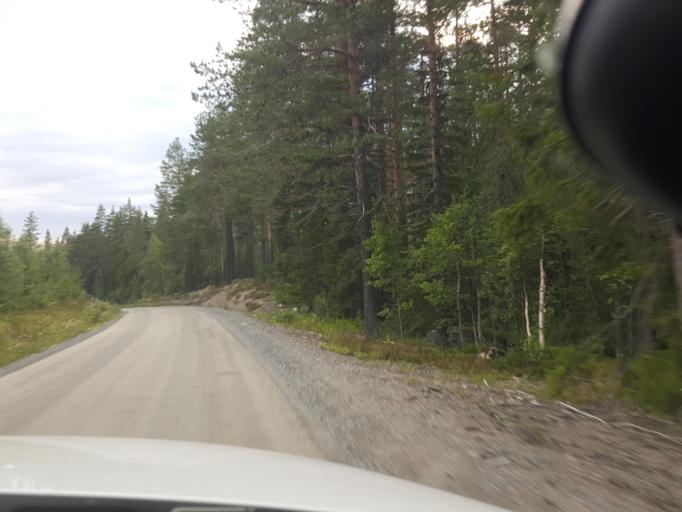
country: SE
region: Vaesternorrland
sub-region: Ange Kommun
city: Ange
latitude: 62.3039
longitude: 15.7199
